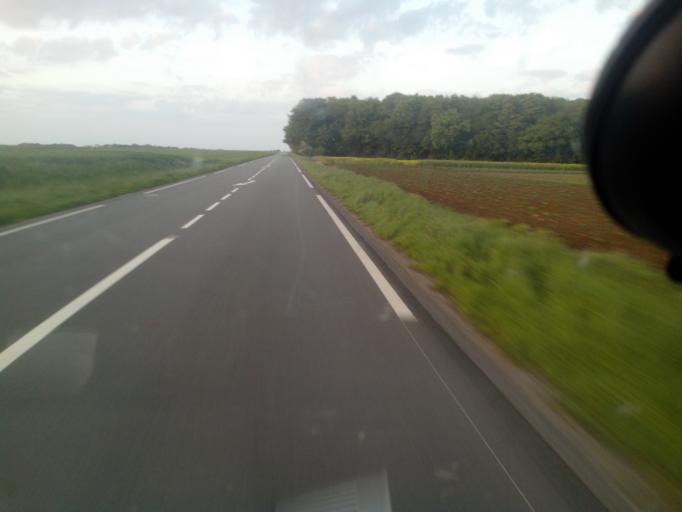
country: FR
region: Picardie
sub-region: Departement de la Somme
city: Crecy-en-Ponthieu
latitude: 50.2153
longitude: 1.9139
